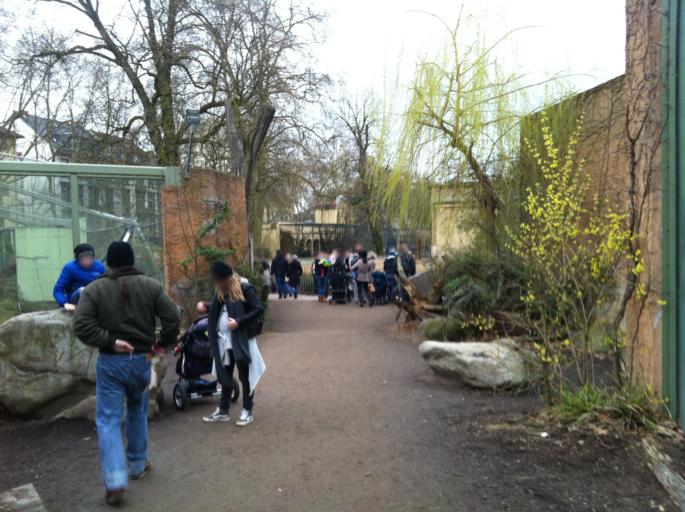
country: DE
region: Hesse
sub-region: Regierungsbezirk Darmstadt
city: Frankfurt am Main
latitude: 50.1157
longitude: 8.7044
